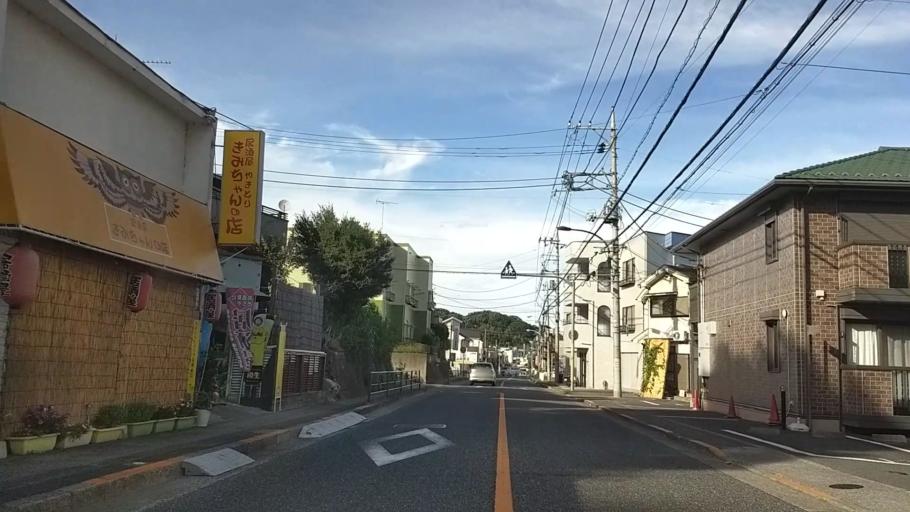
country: JP
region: Tokyo
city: Hachioji
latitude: 35.6357
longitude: 139.3160
